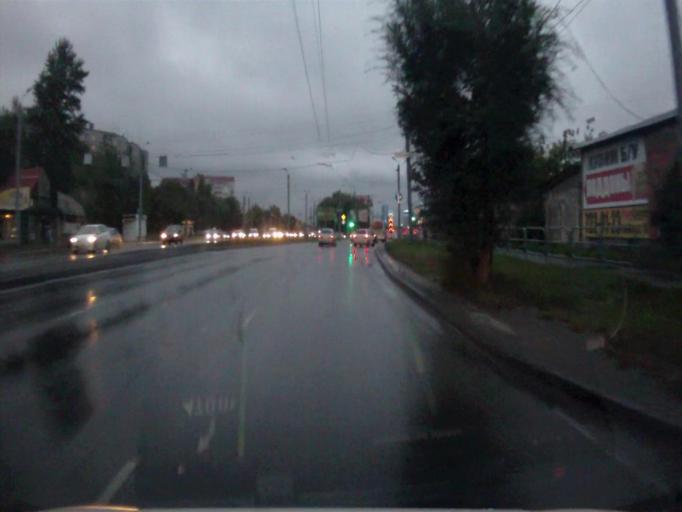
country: RU
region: Chelyabinsk
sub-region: Gorod Chelyabinsk
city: Chelyabinsk
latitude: 55.1420
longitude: 61.4526
